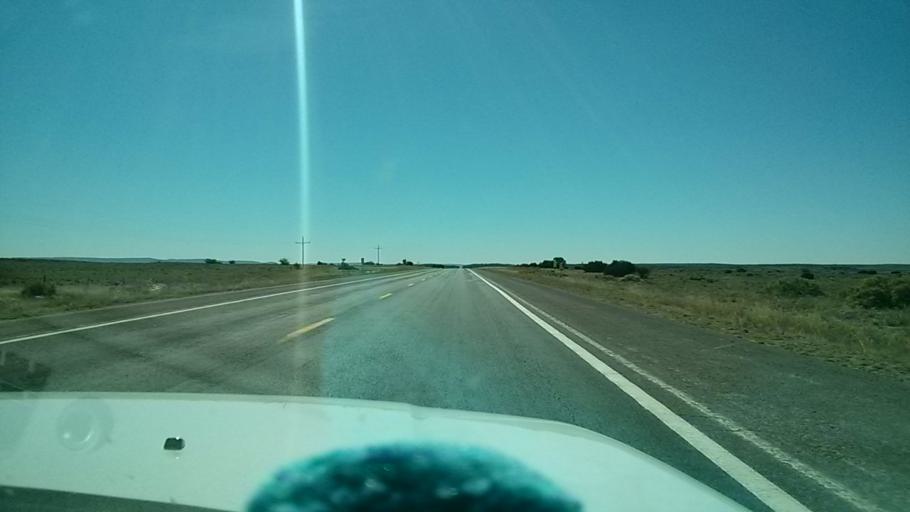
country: US
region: Arizona
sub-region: Mohave County
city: Peach Springs
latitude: 35.5409
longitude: -113.2709
